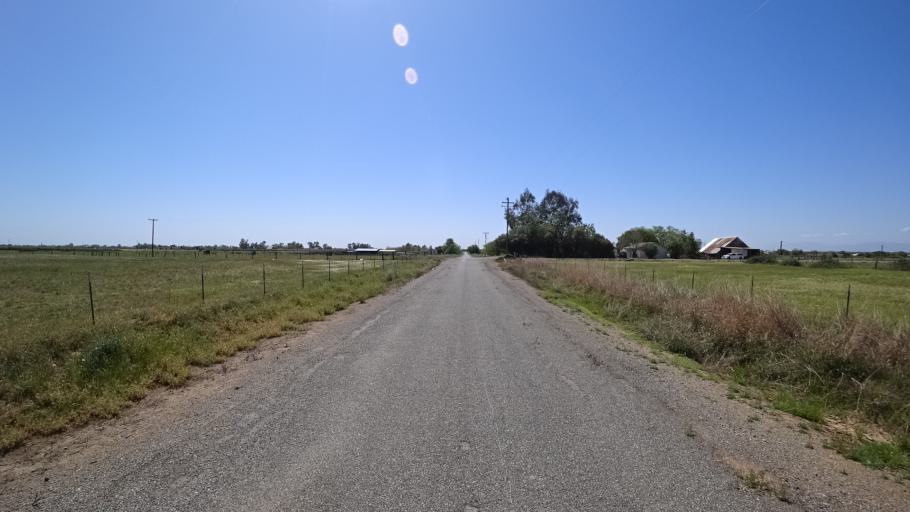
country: US
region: California
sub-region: Glenn County
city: Orland
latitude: 39.7806
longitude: -122.1830
